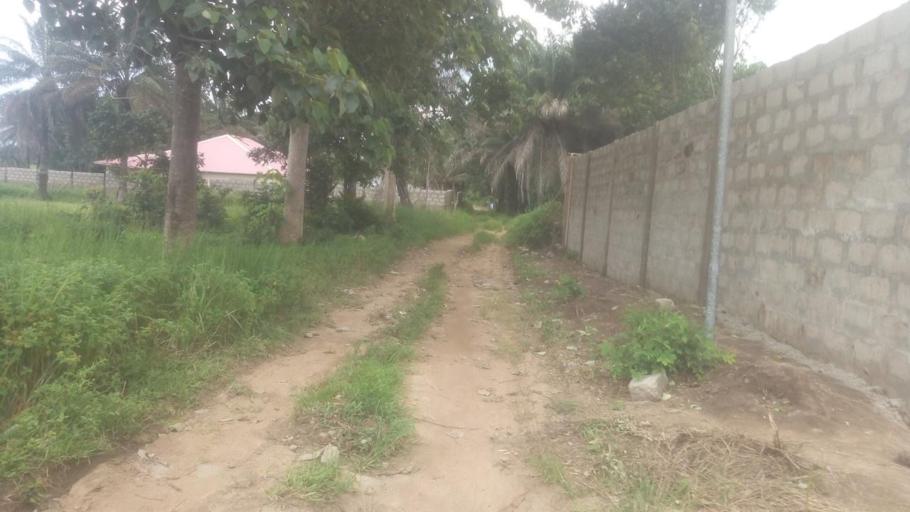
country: SL
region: Northern Province
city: Masoyila
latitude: 8.5621
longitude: -13.1654
